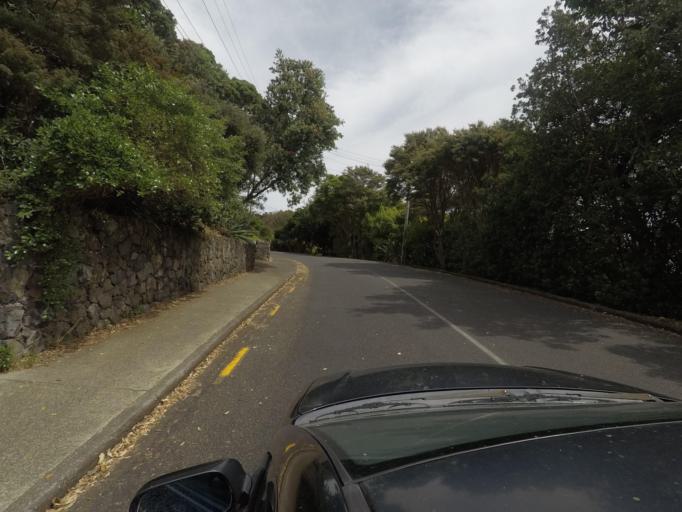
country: NZ
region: Auckland
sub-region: Auckland
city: Rosebank
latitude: -36.8892
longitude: 174.7178
